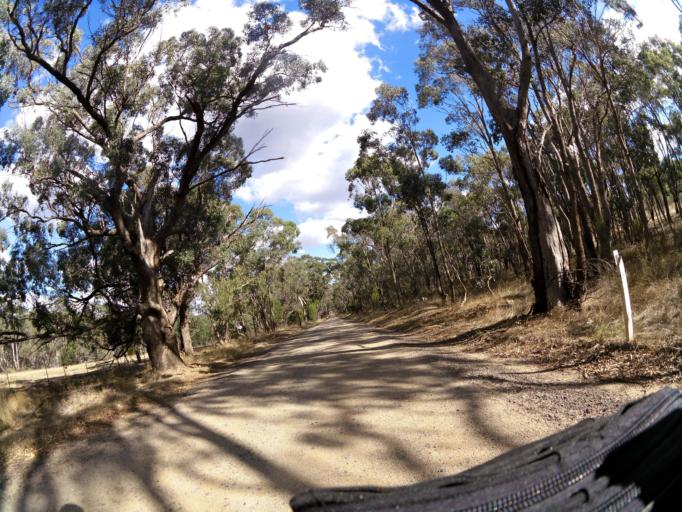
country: AU
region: Victoria
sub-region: Greater Bendigo
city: Kennington
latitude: -36.9992
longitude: 144.8120
